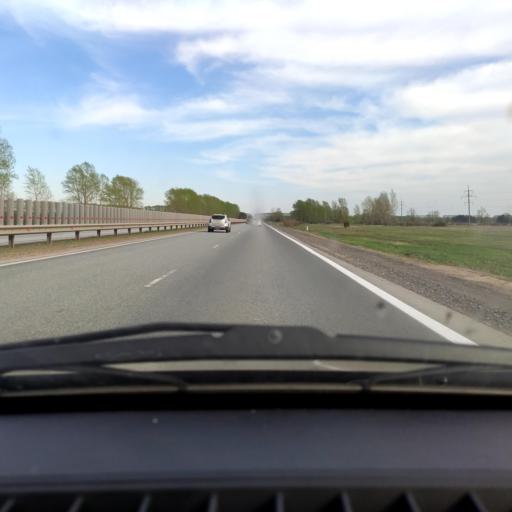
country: RU
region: Bashkortostan
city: Asanovo
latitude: 54.9926
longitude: 55.5103
